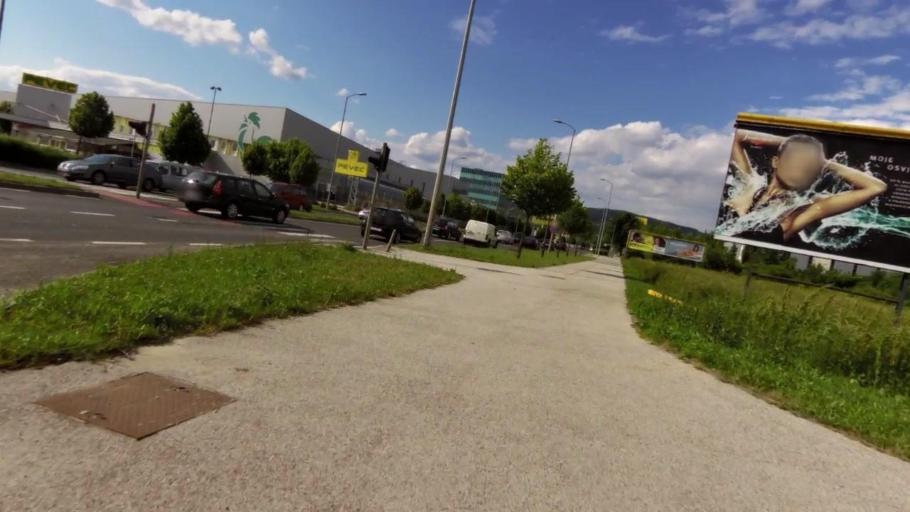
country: HR
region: Grad Zagreb
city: Jezdovec
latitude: 45.8017
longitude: 15.8578
